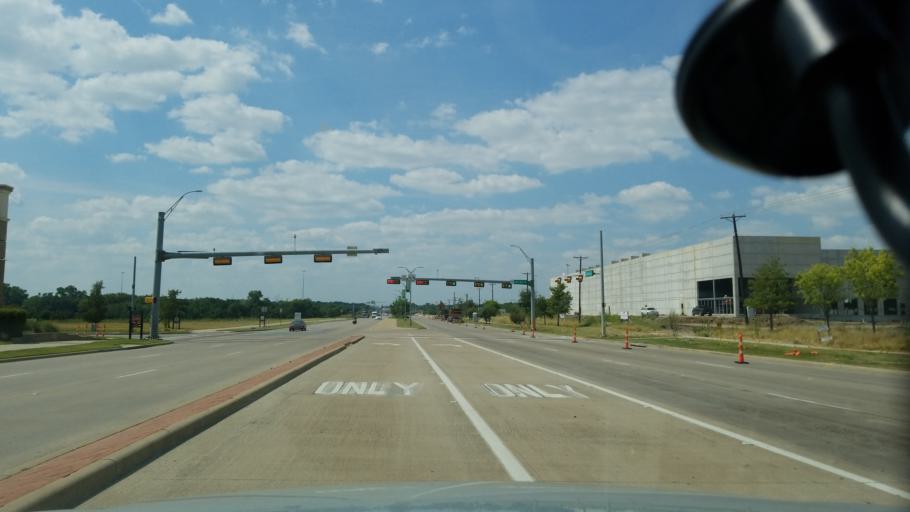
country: US
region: Texas
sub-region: Dallas County
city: Grand Prairie
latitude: 32.7673
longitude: -96.9949
